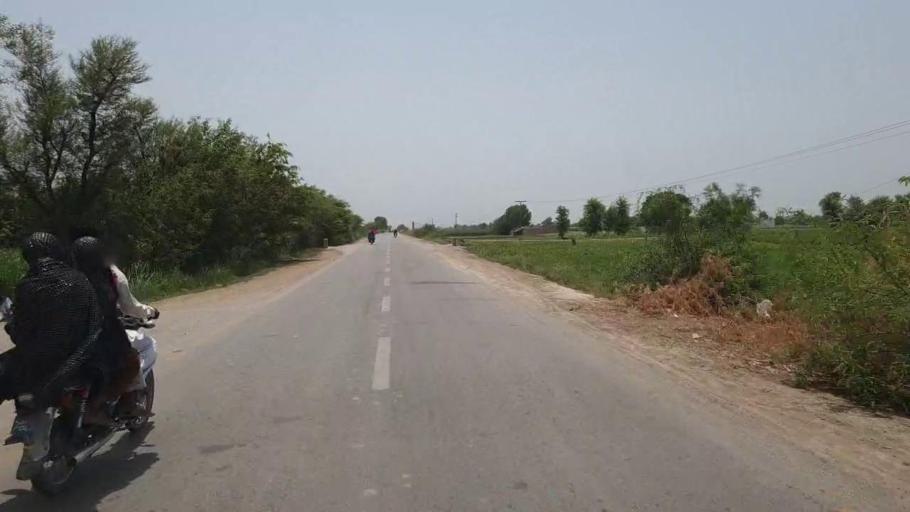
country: PK
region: Sindh
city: Moro
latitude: 26.5998
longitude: 68.0901
